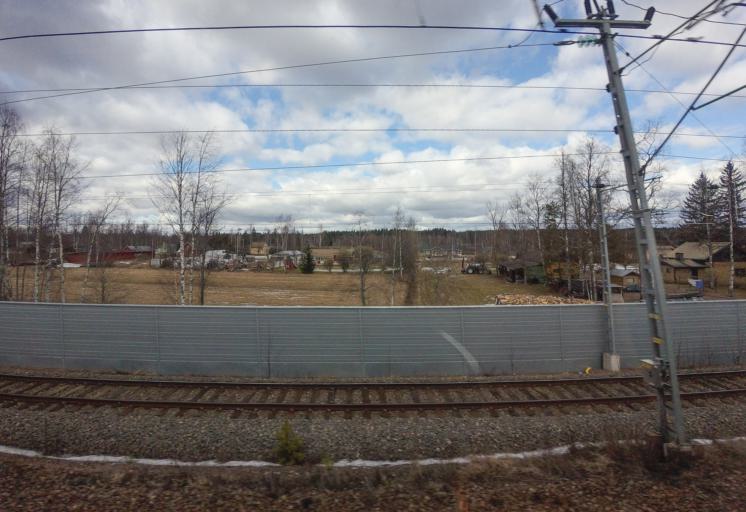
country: FI
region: Kymenlaakso
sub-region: Kouvola
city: Kouvola
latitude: 60.8768
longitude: 26.8414
